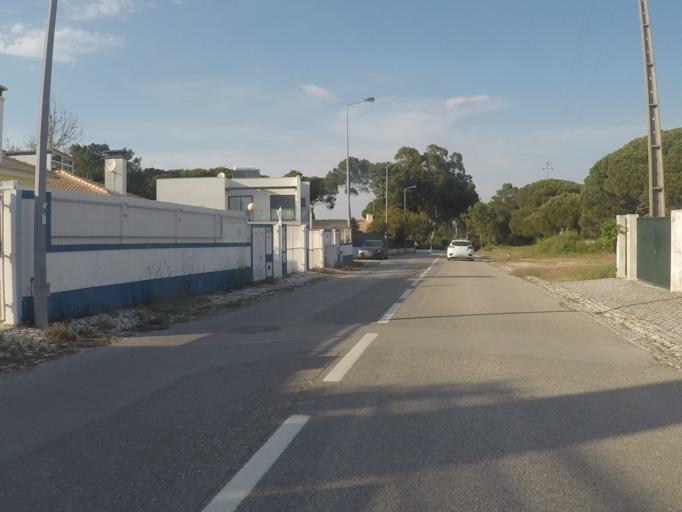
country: PT
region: Setubal
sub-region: Sesimbra
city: Sesimbra
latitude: 38.4675
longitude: -9.1743
